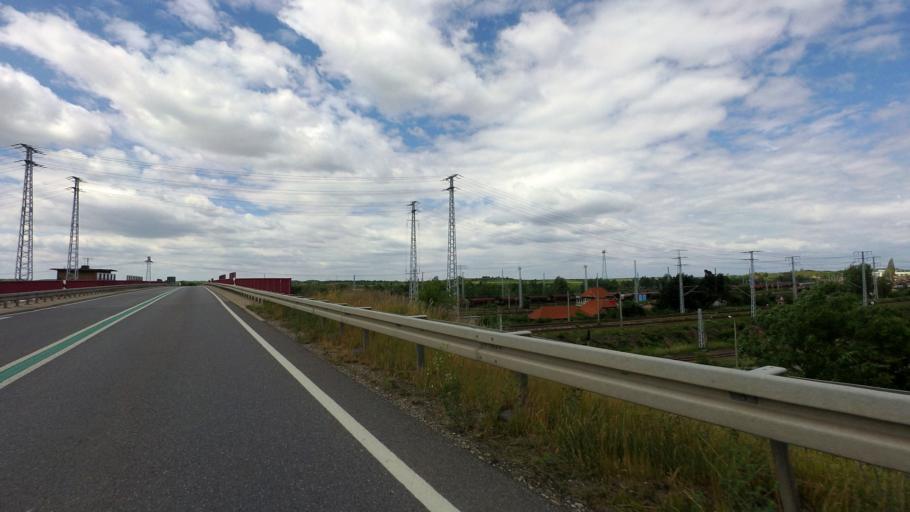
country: DE
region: Brandenburg
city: Senftenberg
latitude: 51.5315
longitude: 14.0153
